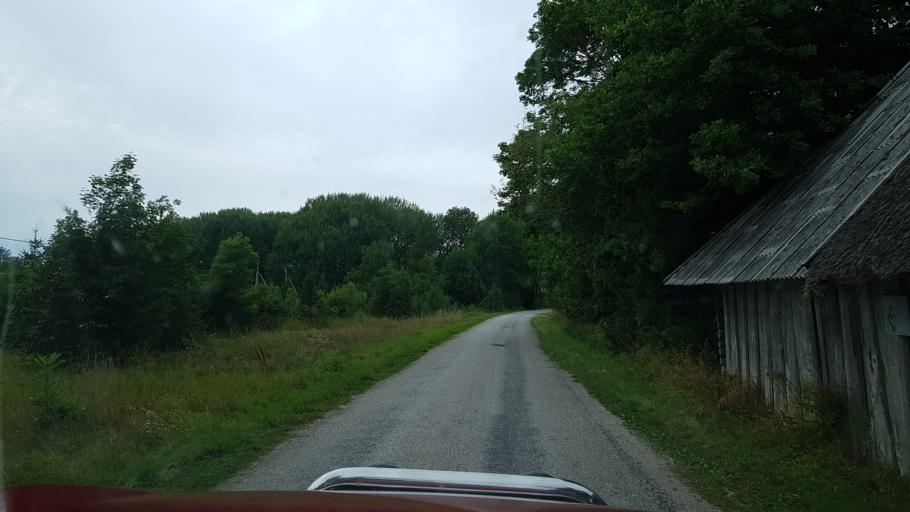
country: EE
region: Laeaene
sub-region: Ridala Parish
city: Uuemoisa
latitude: 58.9891
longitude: 23.6660
